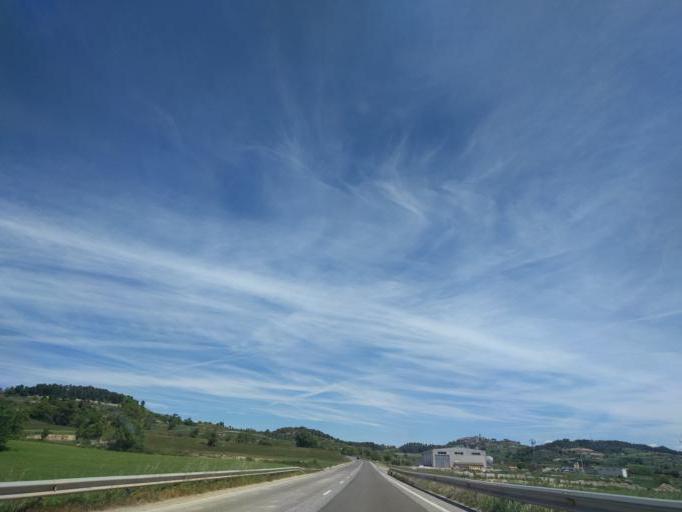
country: ES
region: Catalonia
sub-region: Provincia de Tarragona
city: Santa Coloma de Queralt
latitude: 41.5403
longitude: 1.3976
